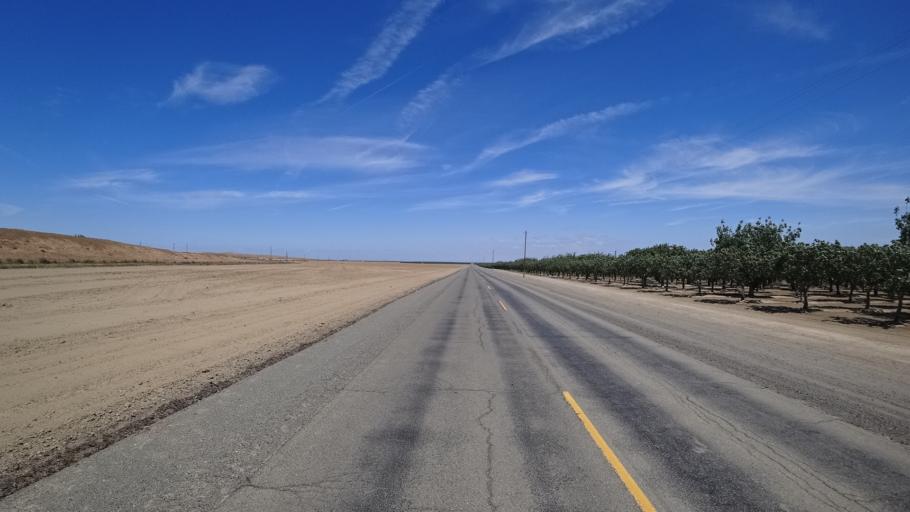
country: US
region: California
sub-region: Kings County
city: Kettleman City
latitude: 35.9107
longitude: -119.9150
